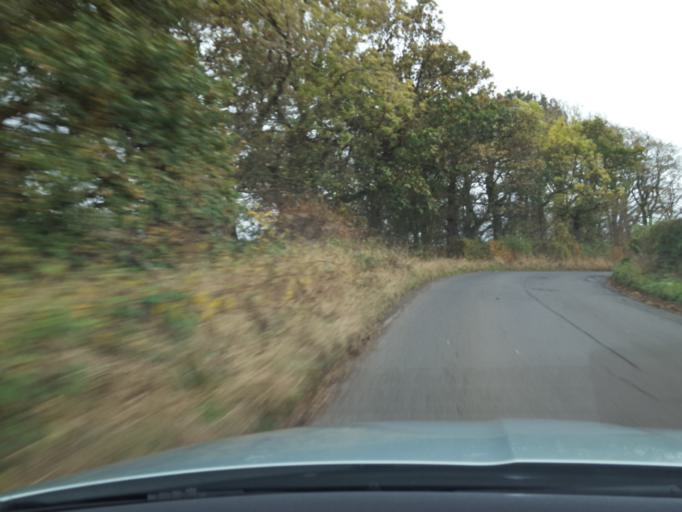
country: GB
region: Scotland
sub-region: West Lothian
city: Kirknewton
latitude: 55.9086
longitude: -3.4367
